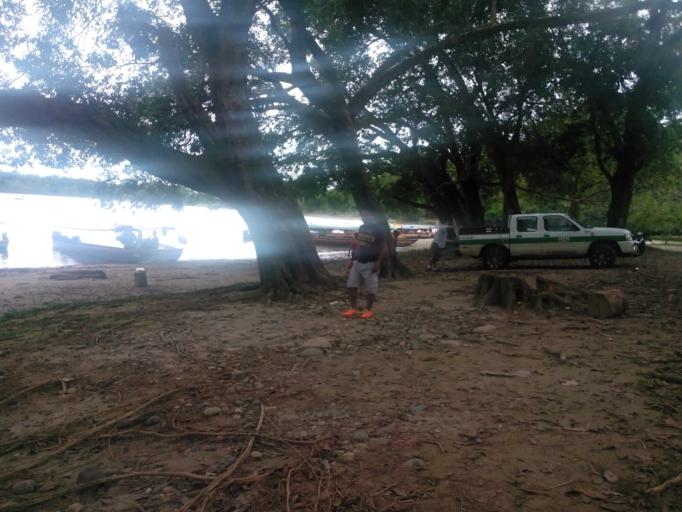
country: EC
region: Napo
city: Tena
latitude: -1.0347
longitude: -77.6652
